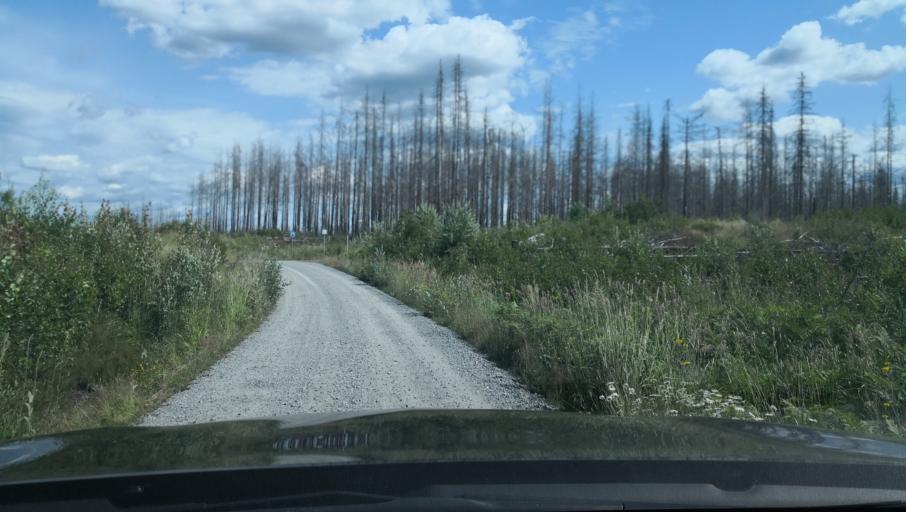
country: SE
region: Vaestmanland
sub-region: Surahammars Kommun
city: Ramnas
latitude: 59.8972
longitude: 16.1236
